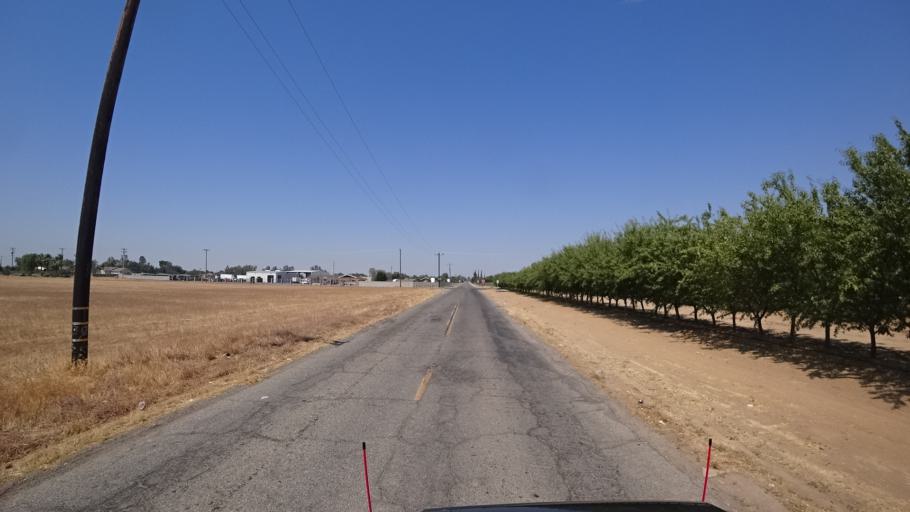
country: US
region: California
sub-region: Fresno County
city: West Park
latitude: 36.7139
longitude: -119.8431
